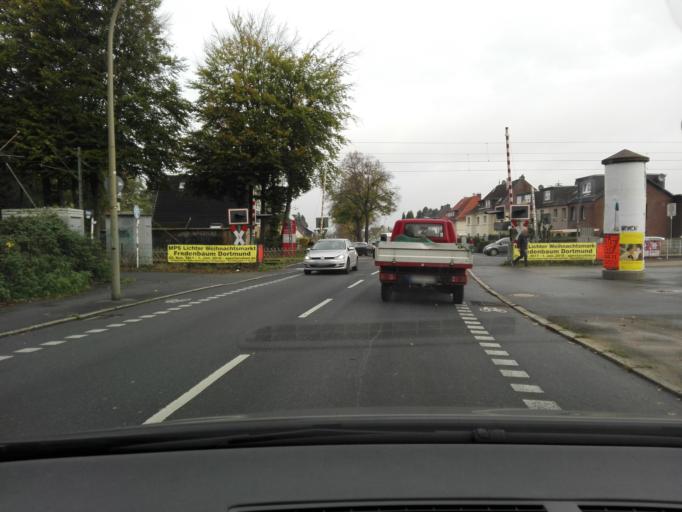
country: DE
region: North Rhine-Westphalia
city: Lanstrop
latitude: 51.5182
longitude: 7.5363
